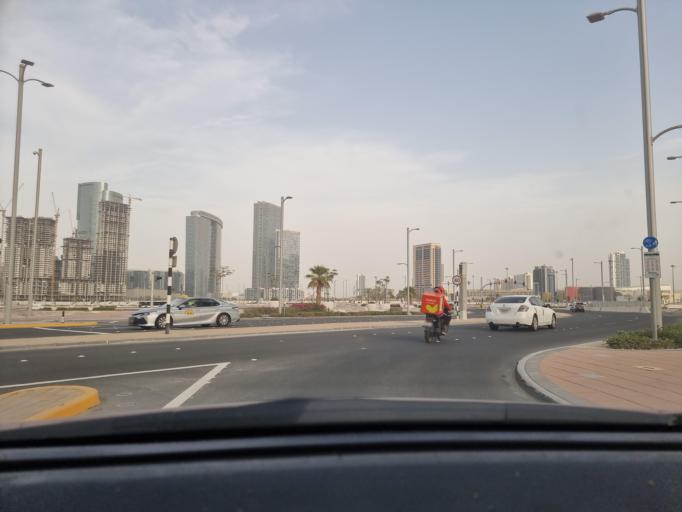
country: AE
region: Abu Dhabi
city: Abu Dhabi
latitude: 24.4981
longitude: 54.3955
